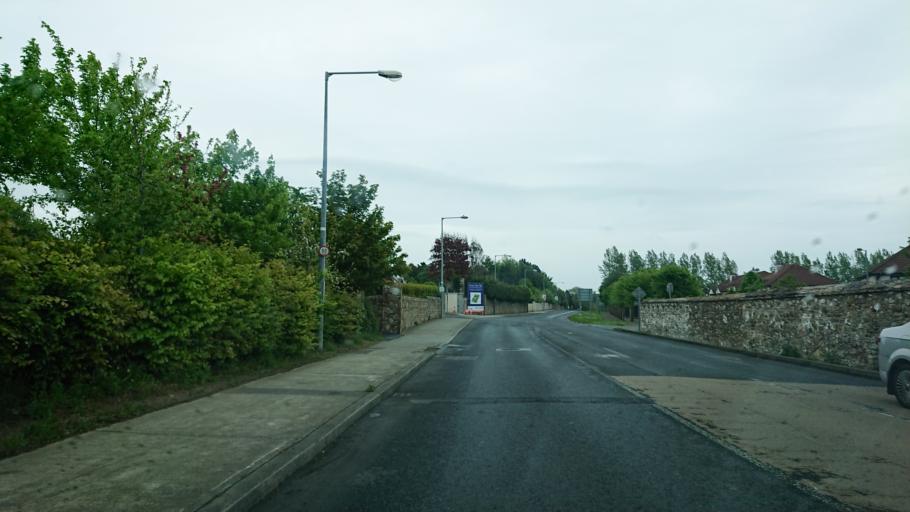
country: IE
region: Munster
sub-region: Waterford
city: Waterford
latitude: 52.2408
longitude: -7.0890
